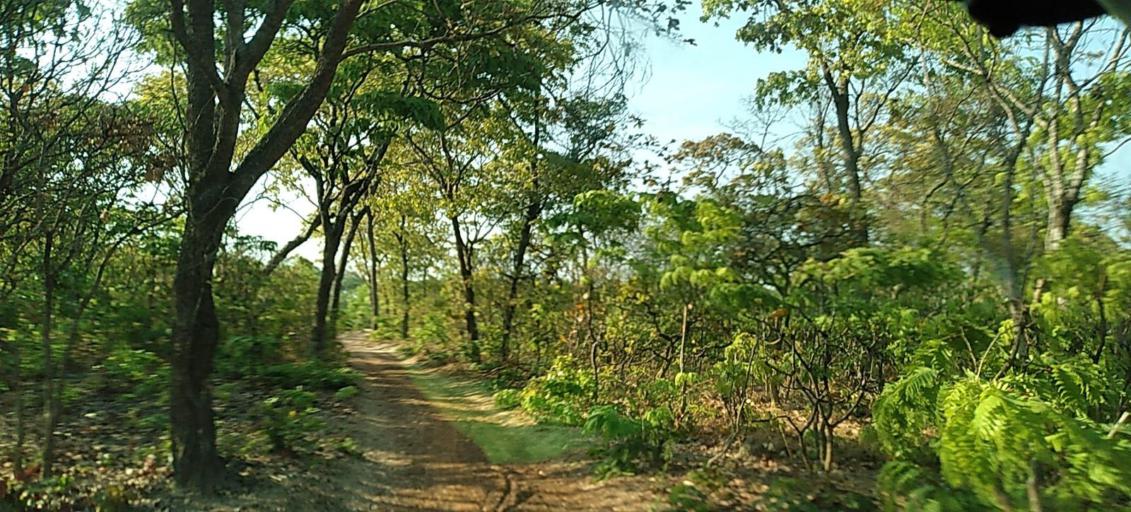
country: ZM
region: North-Western
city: Kalengwa
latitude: -13.1738
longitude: 25.0380
